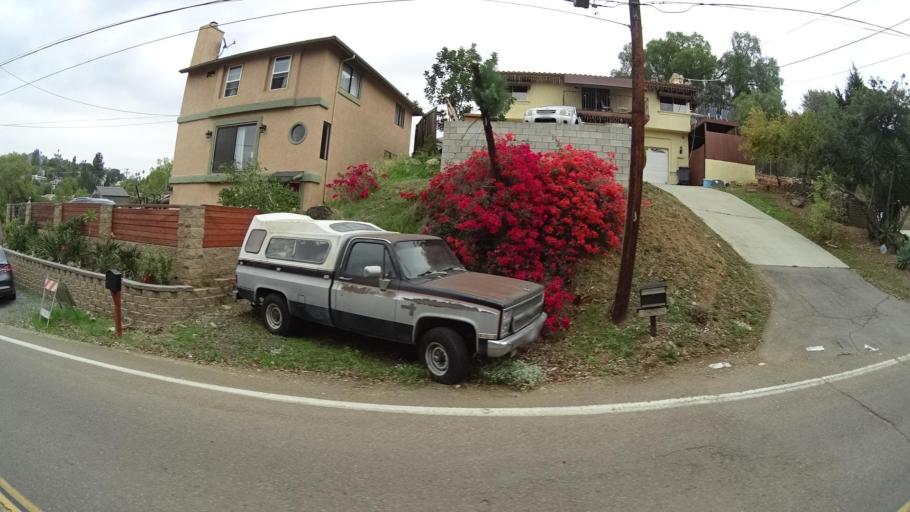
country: US
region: California
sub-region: San Diego County
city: Spring Valley
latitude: 32.7490
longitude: -116.9987
